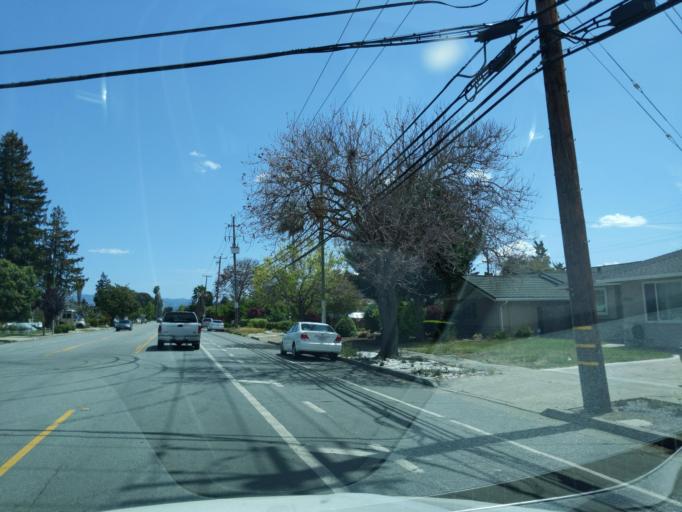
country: US
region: California
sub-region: Santa Clara County
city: Campbell
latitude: 37.3088
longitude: -121.9600
